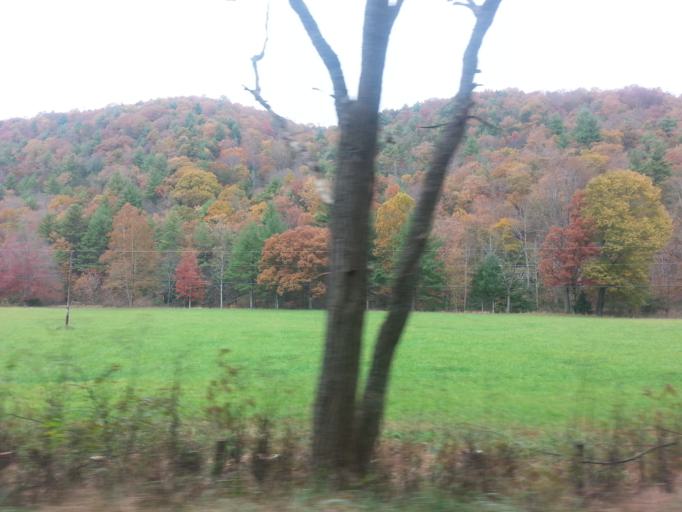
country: US
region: Virginia
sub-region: Bland County
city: Bland
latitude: 37.0763
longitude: -80.9554
